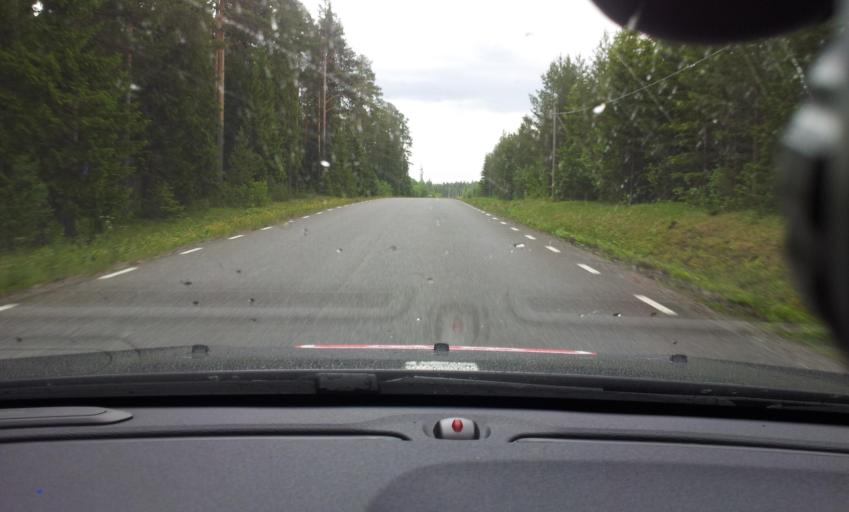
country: SE
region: Jaemtland
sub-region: OEstersunds Kommun
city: Brunflo
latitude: 63.1779
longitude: 14.9304
